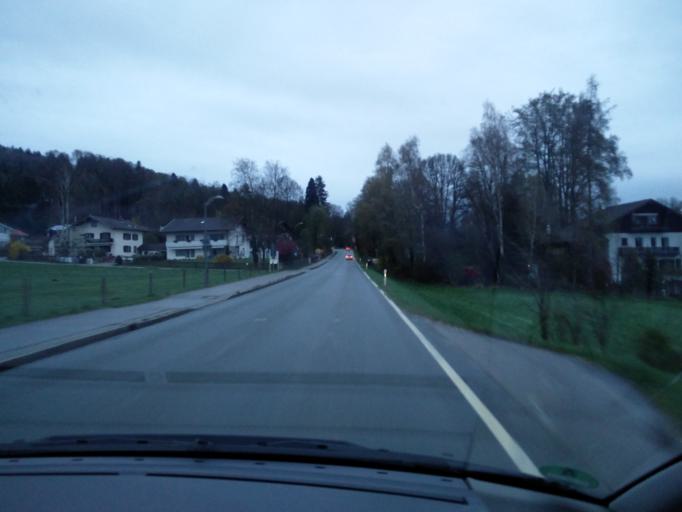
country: DE
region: Bavaria
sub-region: Upper Bavaria
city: Prien am Chiemsee
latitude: 47.8575
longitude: 12.3401
